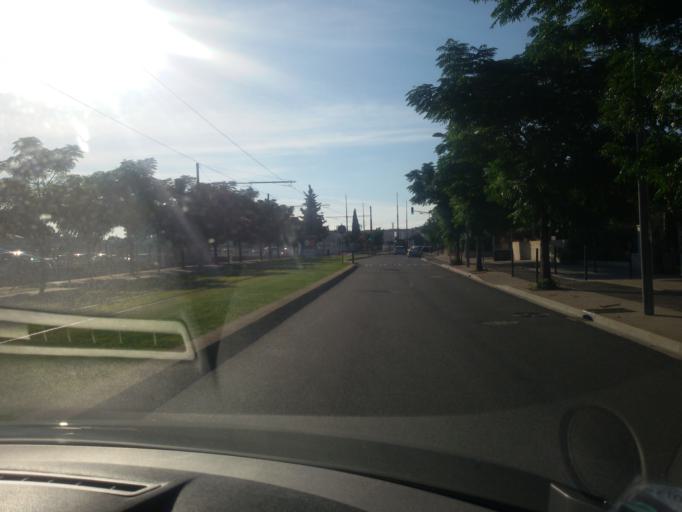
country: FR
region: Languedoc-Roussillon
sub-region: Departement de l'Herault
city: Montpellier
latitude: 43.5898
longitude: 3.8870
